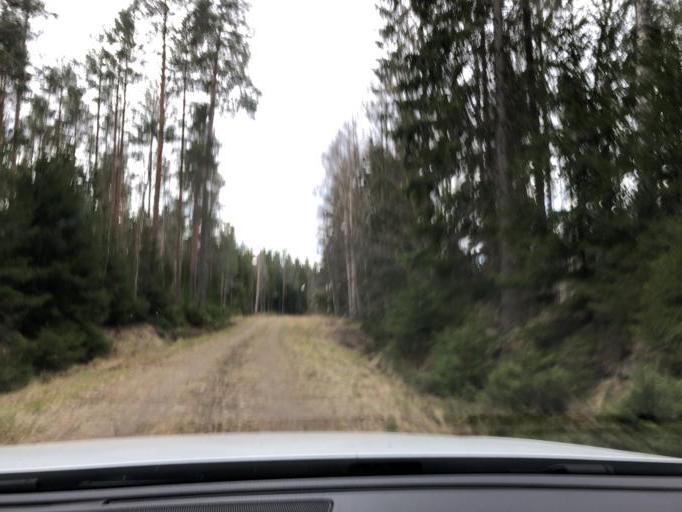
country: SE
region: Gaevleborg
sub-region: Gavle Kommun
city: Hedesunda
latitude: 60.3379
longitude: 17.0633
